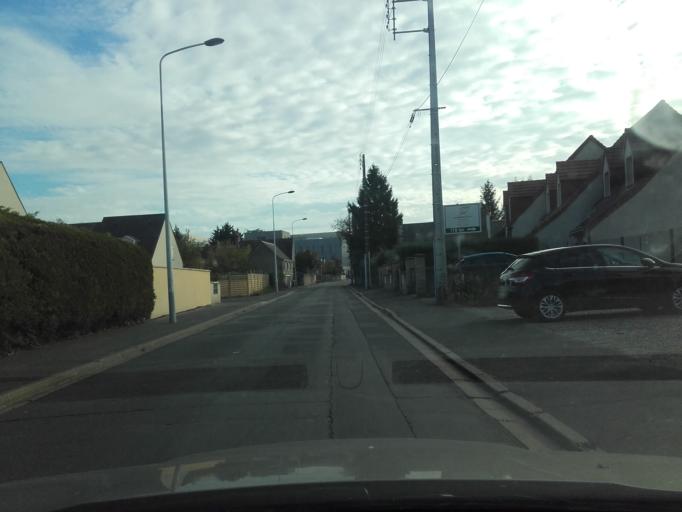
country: FR
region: Centre
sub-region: Departement d'Indre-et-Loire
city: Saint-Cyr-sur-Loire
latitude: 47.4212
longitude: 0.6976
